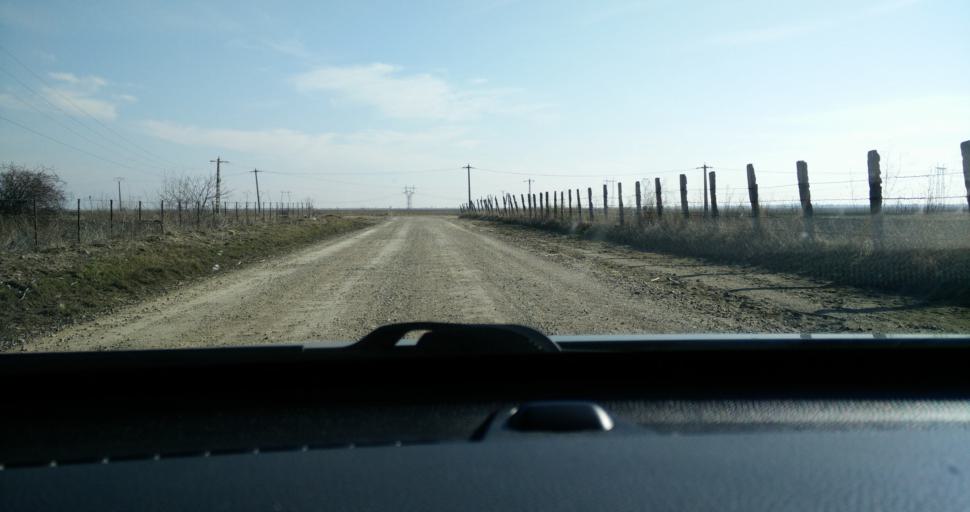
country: RO
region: Vrancea
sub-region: Comuna Suraia
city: Suraia
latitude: 45.6601
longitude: 27.3967
